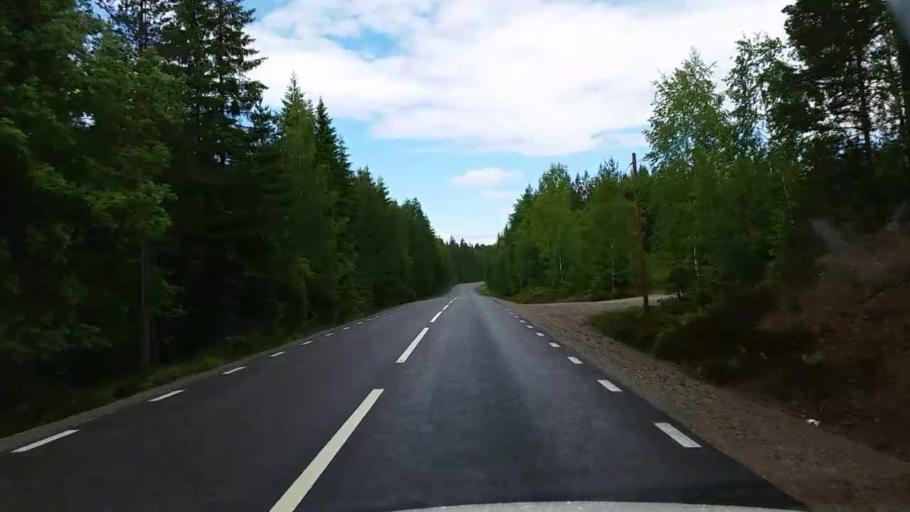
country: SE
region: Gaevleborg
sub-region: Sandvikens Kommun
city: Jarbo
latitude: 60.8503
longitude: 16.4505
